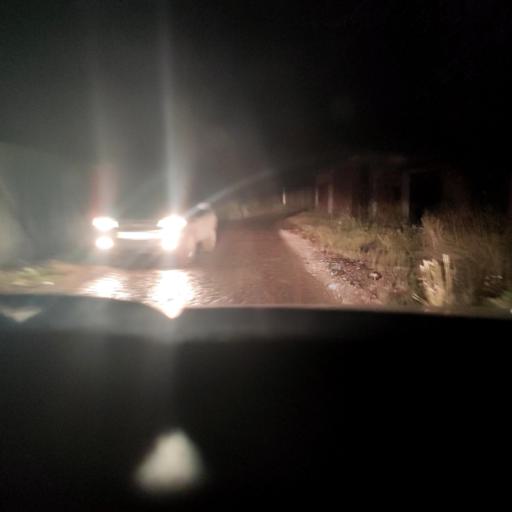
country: RU
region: Perm
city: Froly
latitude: 57.9516
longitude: 56.2464
